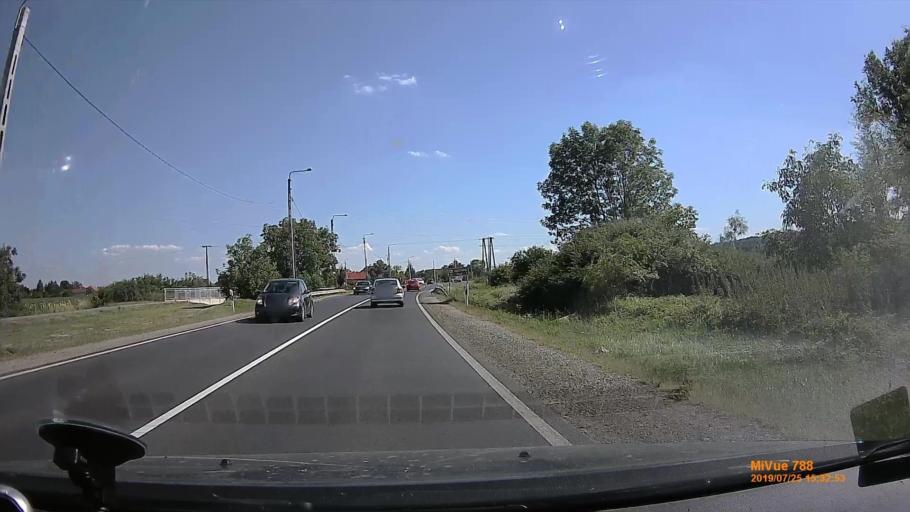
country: HU
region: Borsod-Abauj-Zemplen
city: Malyi
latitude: 48.0014
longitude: 20.8313
